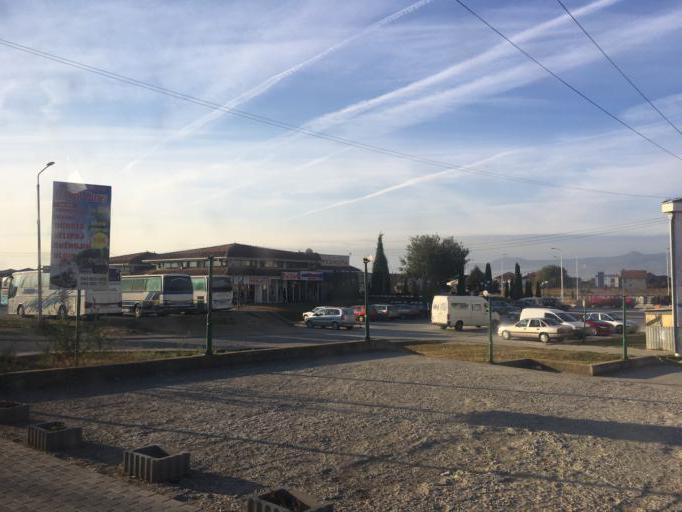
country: XK
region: Pristina
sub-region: Komuna e Drenasit
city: Glogovac
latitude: 42.6216
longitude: 20.8925
